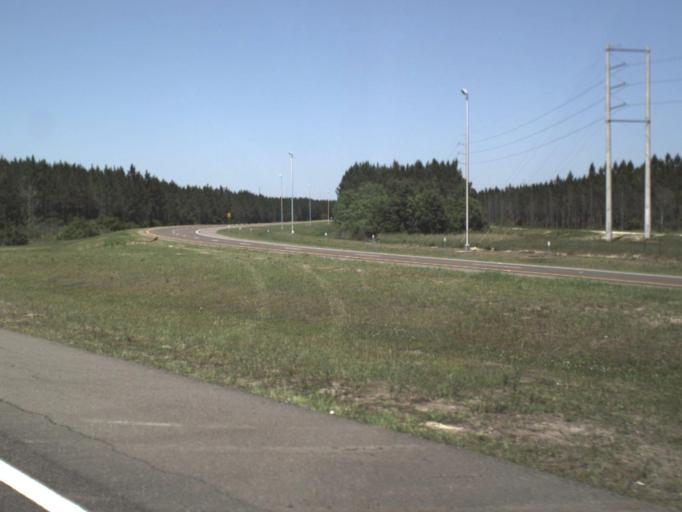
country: US
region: Florida
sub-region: Duval County
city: Baldwin
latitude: 30.3000
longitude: -81.8783
